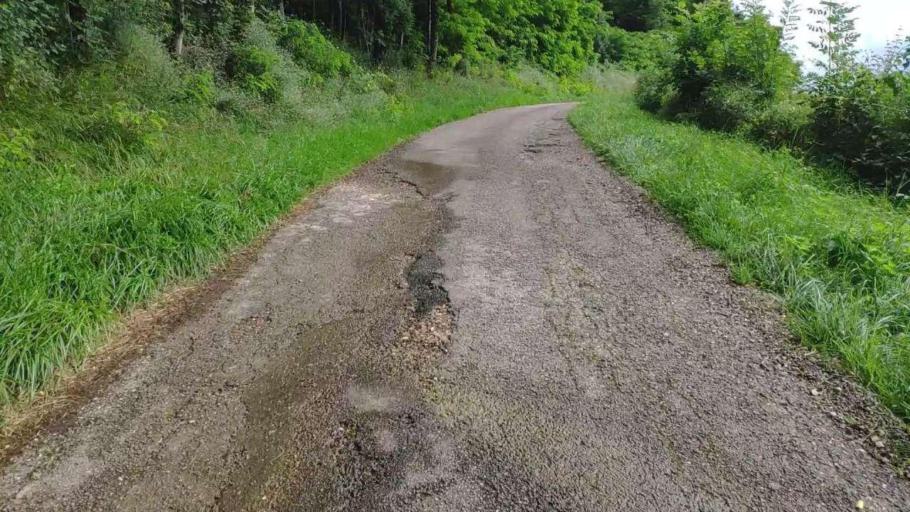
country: FR
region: Franche-Comte
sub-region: Departement du Jura
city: Poligny
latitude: 46.8285
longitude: 5.5904
